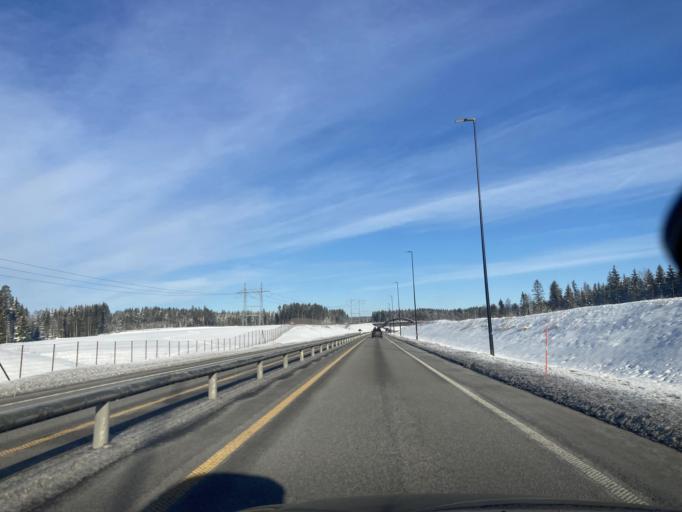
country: NO
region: Hedmark
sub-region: Loten
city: Loten
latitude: 60.8125
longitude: 11.2861
